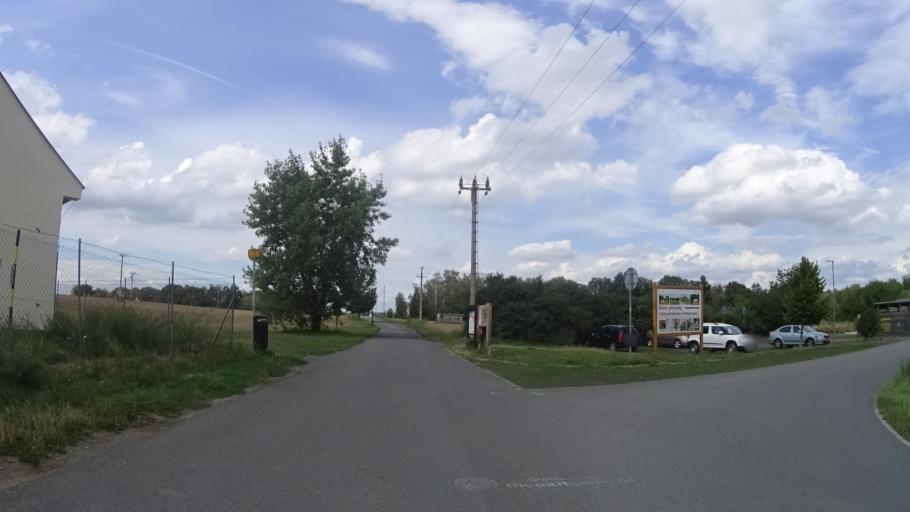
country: CZ
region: Olomoucky
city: Horka nad Moravou
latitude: 49.6407
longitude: 17.1986
